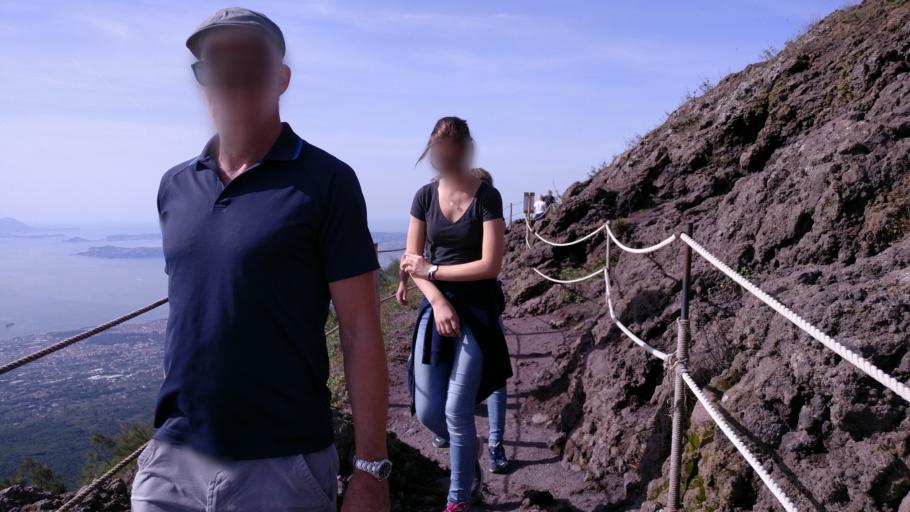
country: IT
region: Campania
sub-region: Provincia di Napoli
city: Torre del Greco
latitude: 40.8188
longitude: 14.4255
